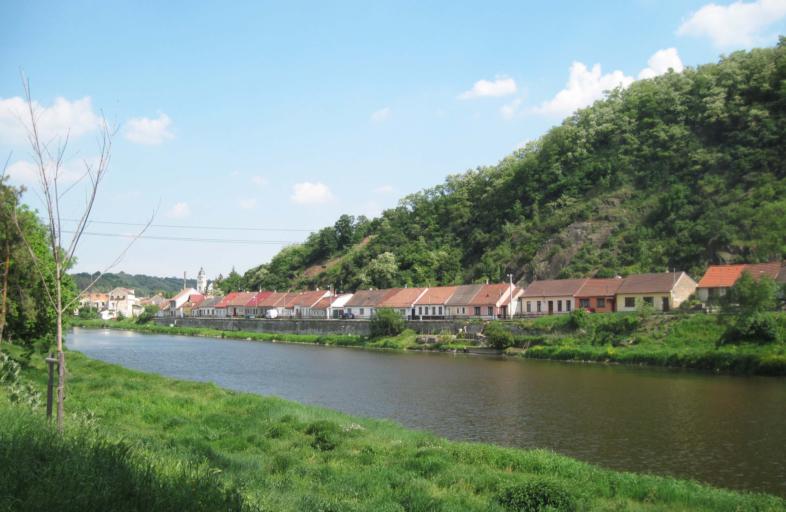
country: CZ
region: South Moravian
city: Dolni Kounice
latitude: 49.0712
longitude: 16.4584
